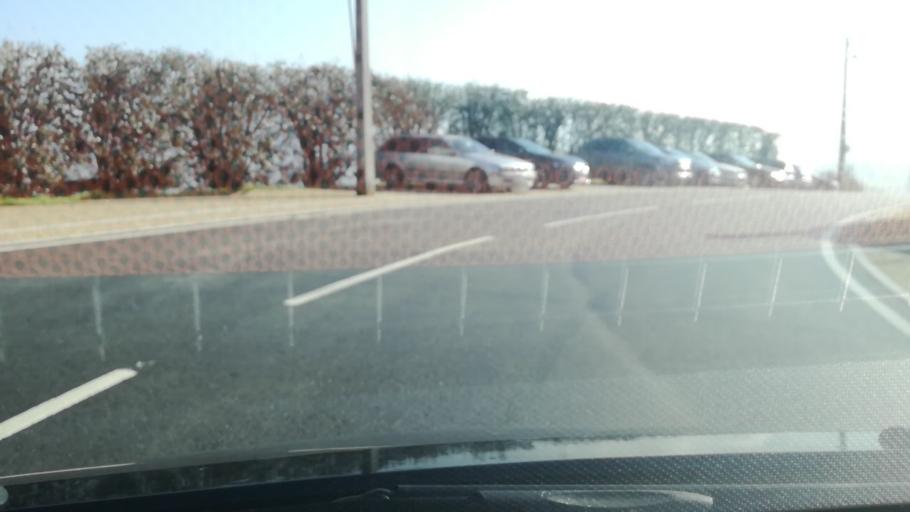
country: PT
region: Braga
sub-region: Guimaraes
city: Ponte
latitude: 41.5278
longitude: -8.3408
